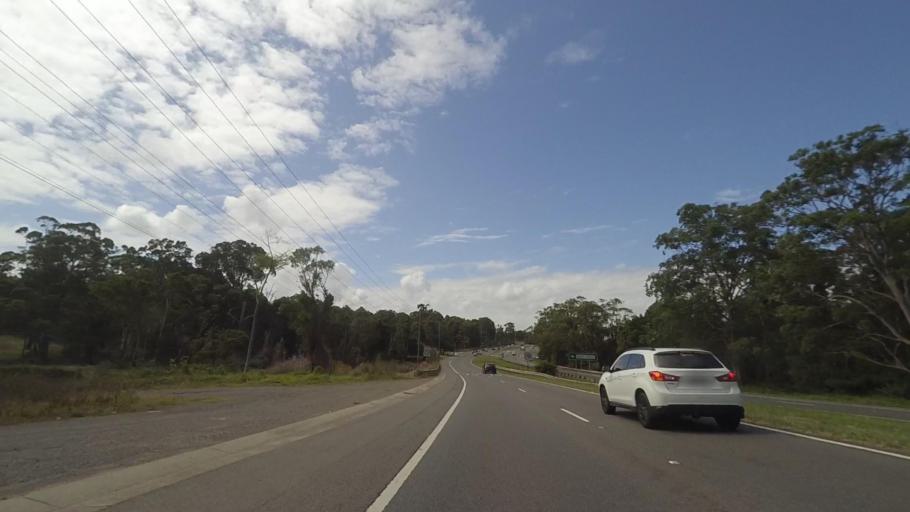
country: AU
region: New South Wales
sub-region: Lake Macquarie Shire
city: Windale
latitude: -33.0013
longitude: 151.6859
